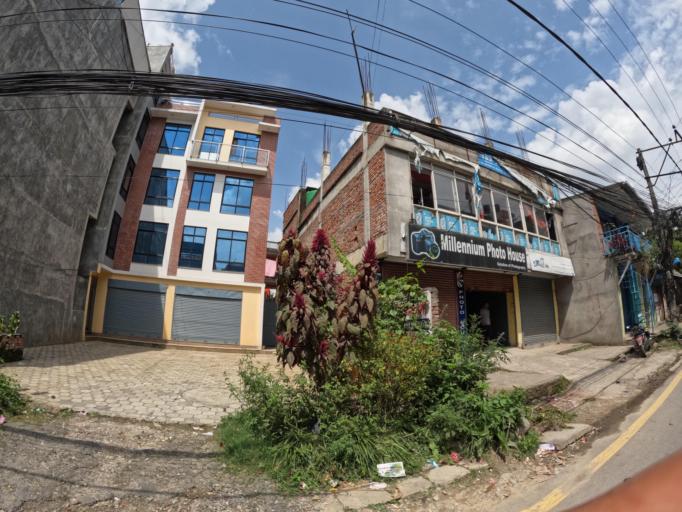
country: NP
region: Central Region
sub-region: Bagmati Zone
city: Bhaktapur
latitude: 27.6798
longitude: 85.3762
